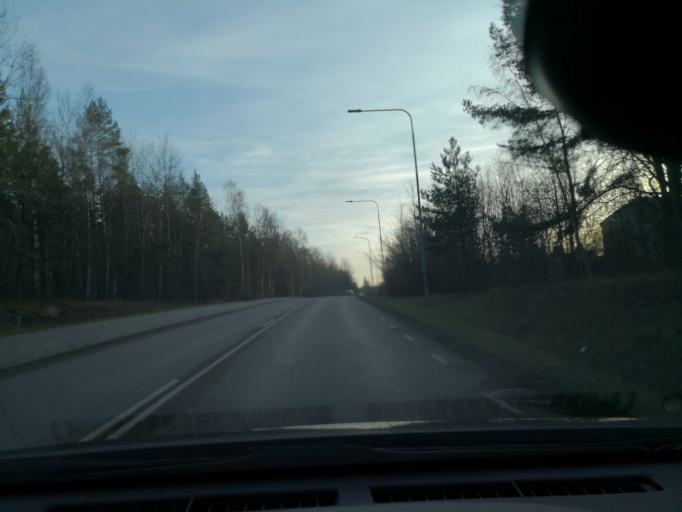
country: SE
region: Vaestmanland
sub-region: Vasteras
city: Vasteras
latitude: 59.6151
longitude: 16.5059
